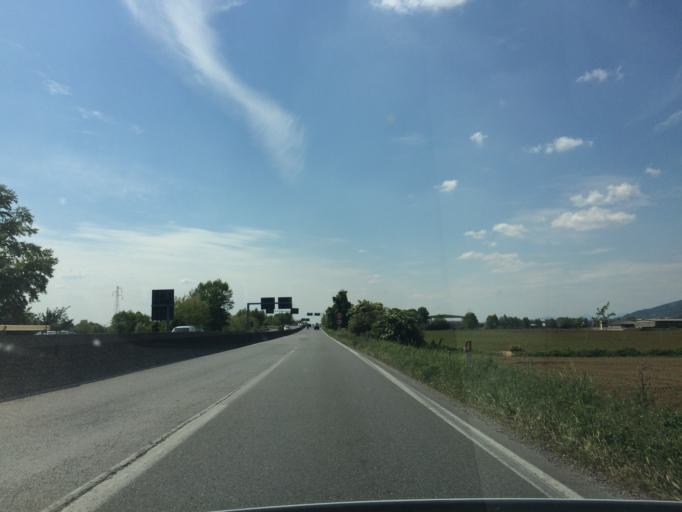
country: IT
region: Lombardy
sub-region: Provincia di Brescia
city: Rezzato
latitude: 45.4969
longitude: 10.3159
